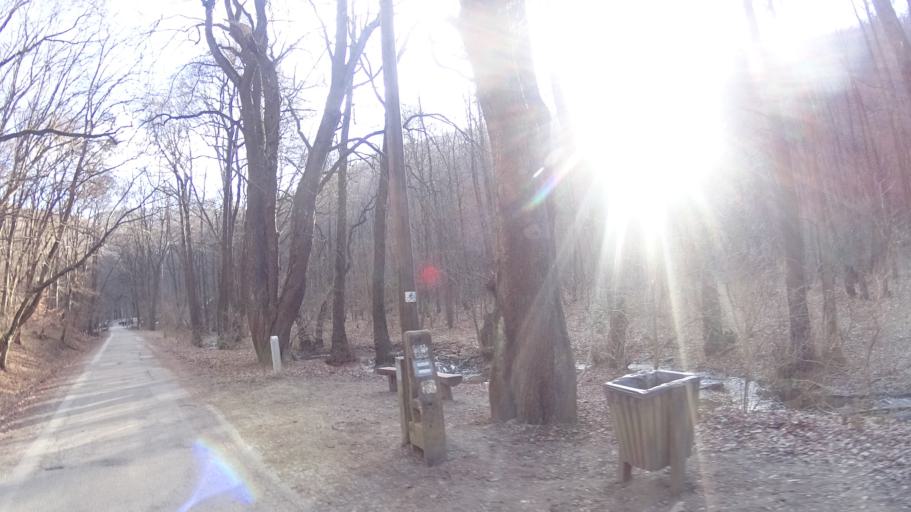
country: HU
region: Heves
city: Szilvasvarad
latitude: 48.0907
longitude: 20.4008
